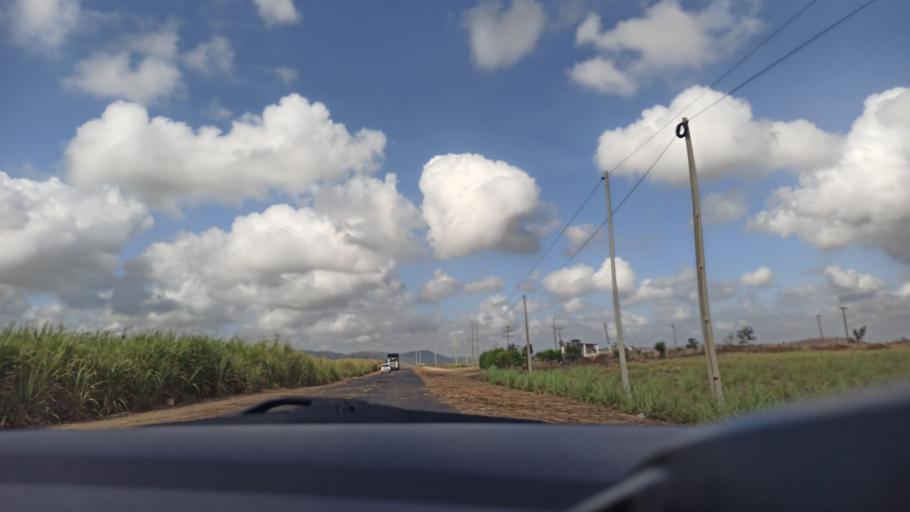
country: BR
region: Paraiba
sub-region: Juripiranga
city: Juripiranga
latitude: -7.3854
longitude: -35.2490
